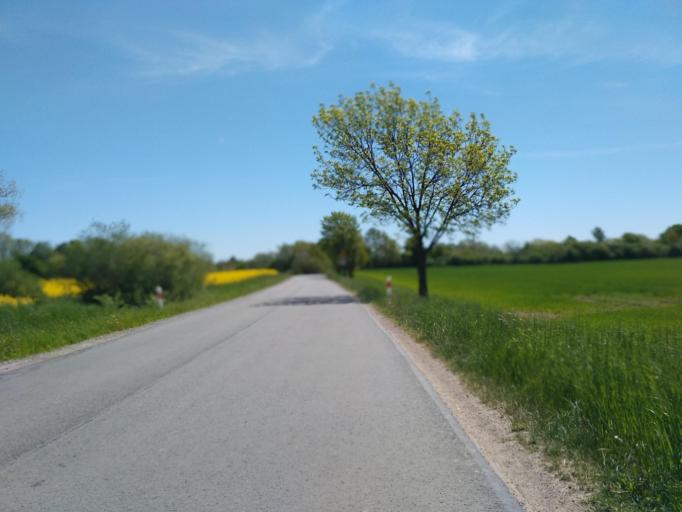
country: PL
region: Subcarpathian Voivodeship
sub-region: Powiat krosnienski
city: Sieniawa
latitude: 49.5458
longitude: 21.9481
